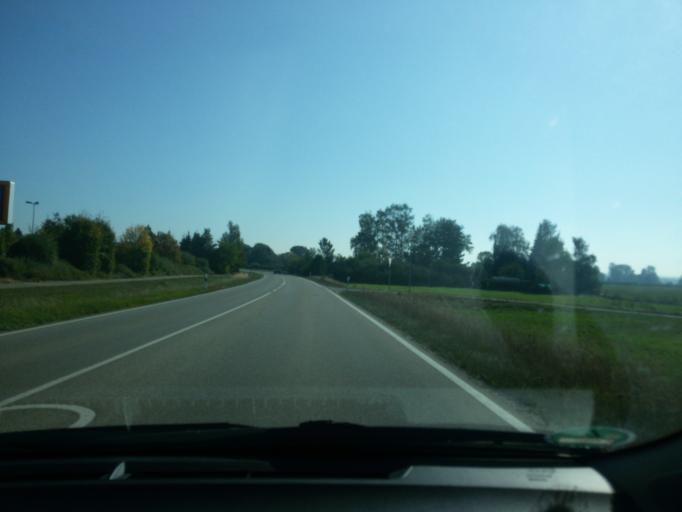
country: DE
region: Bavaria
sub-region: Regierungsbezirk Mittelfranken
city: Wassertrudingen
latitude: 49.0417
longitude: 10.5848
